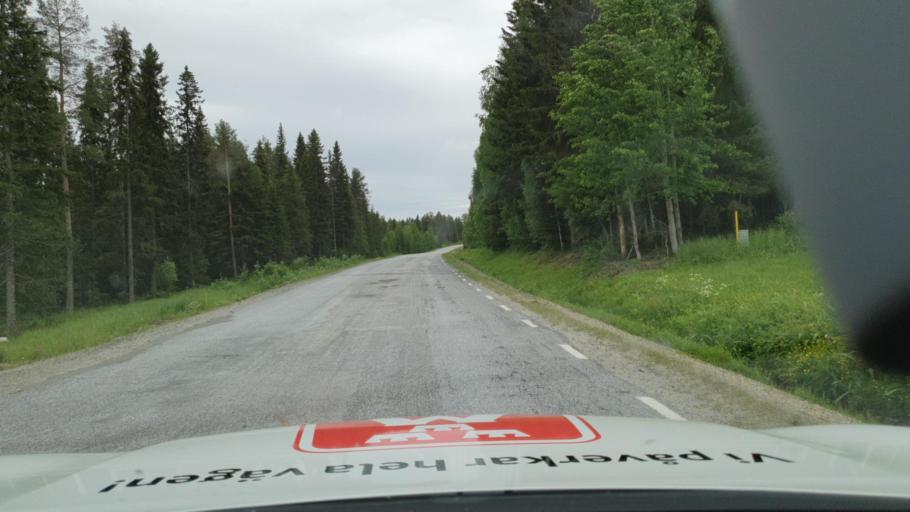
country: SE
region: Vaesterbotten
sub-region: Lycksele Kommun
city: Lycksele
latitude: 64.1371
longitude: 18.3609
